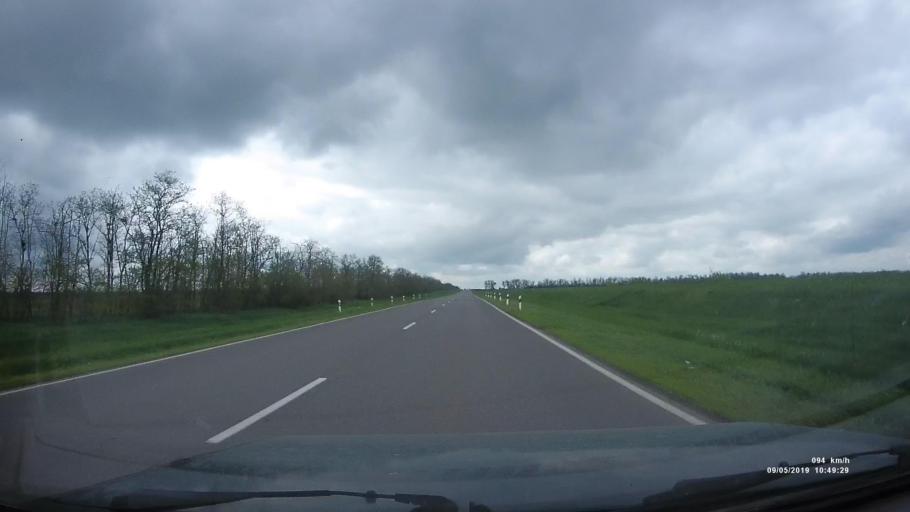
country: RU
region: Rostov
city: Peshkovo
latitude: 46.9412
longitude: 39.3566
